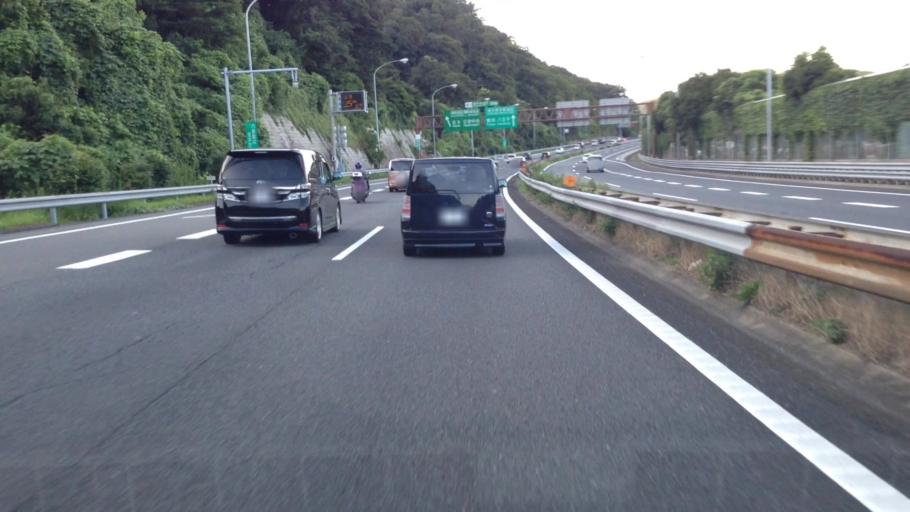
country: JP
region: Kanagawa
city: Zushi
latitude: 35.3406
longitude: 139.5907
